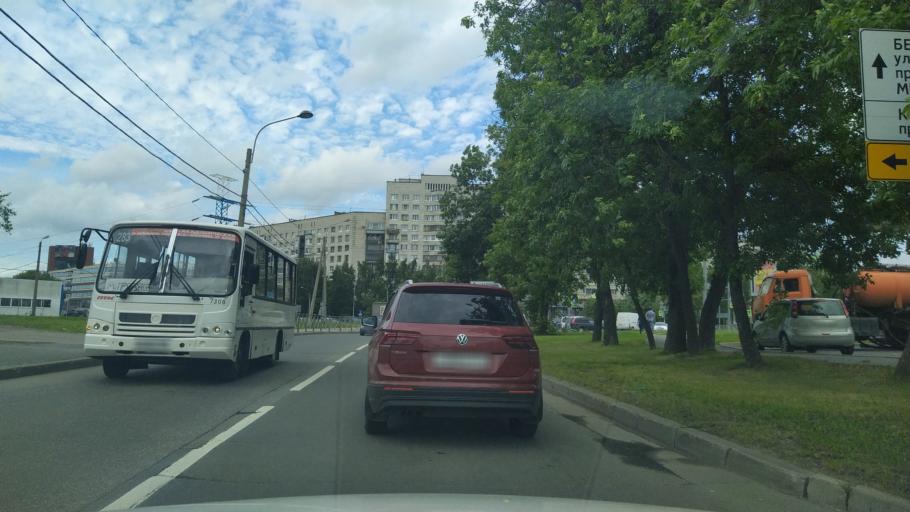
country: RU
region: Leningrad
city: Kalininskiy
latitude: 59.9786
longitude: 30.3822
